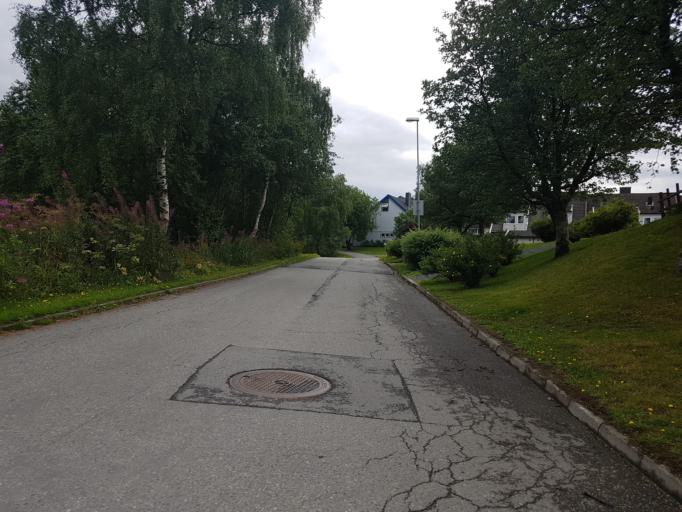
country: NO
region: Sor-Trondelag
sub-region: Trondheim
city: Trondheim
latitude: 63.3856
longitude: 10.4038
